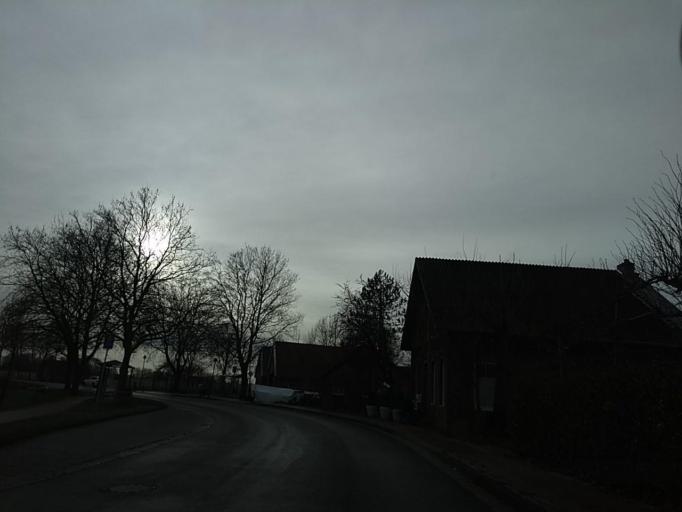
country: DE
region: Lower Saxony
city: Jemgum
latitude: 53.3080
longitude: 7.3355
